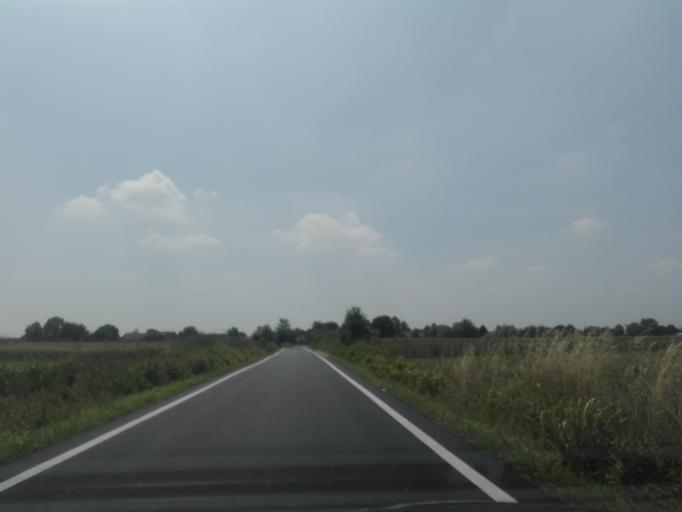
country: IT
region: Veneto
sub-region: Provincia di Rovigo
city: Grignano Polesine
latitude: 45.0517
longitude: 11.7519
